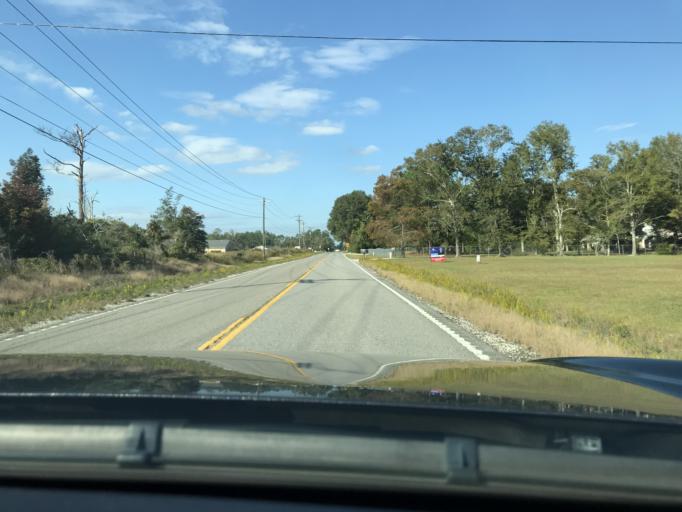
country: US
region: Louisiana
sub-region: Calcasieu Parish
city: Moss Bluff
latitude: 30.3201
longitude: -93.2582
